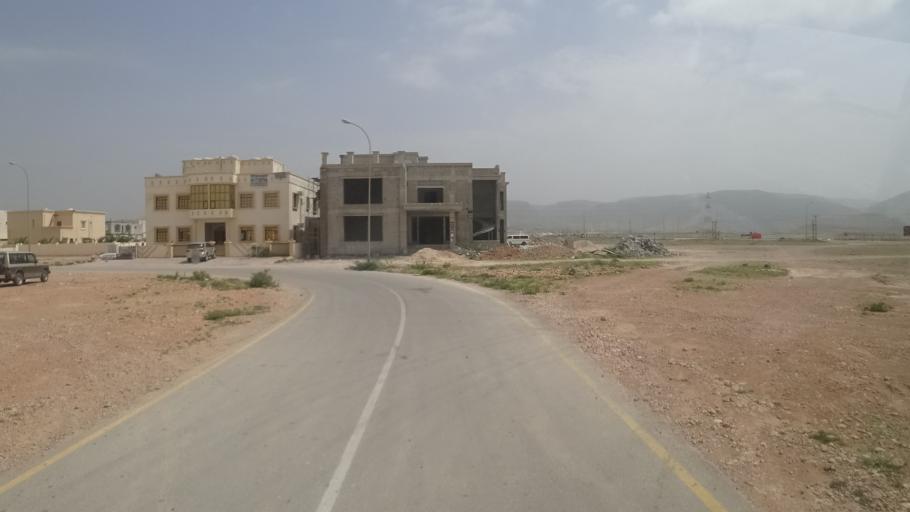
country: OM
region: Zufar
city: Salalah
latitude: 17.0996
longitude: 54.2157
